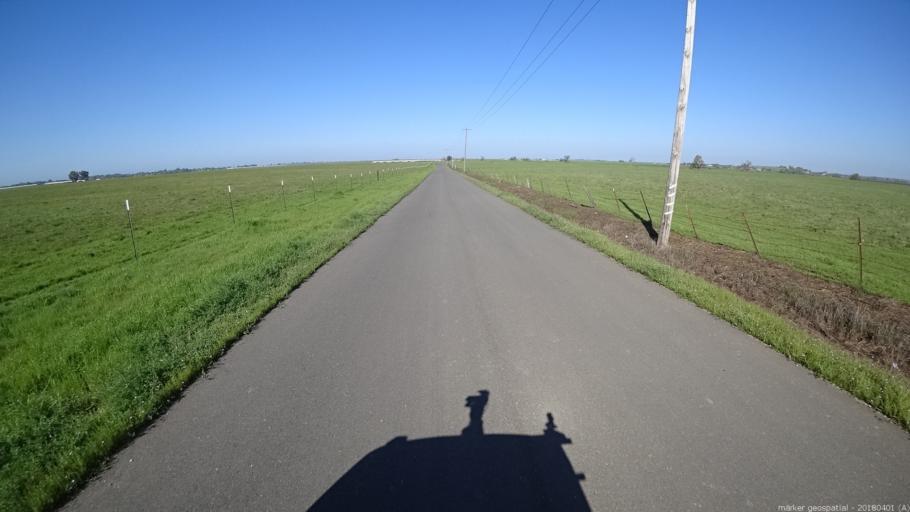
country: US
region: California
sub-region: Sacramento County
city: Rancho Murieta
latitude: 38.4659
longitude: -121.1464
